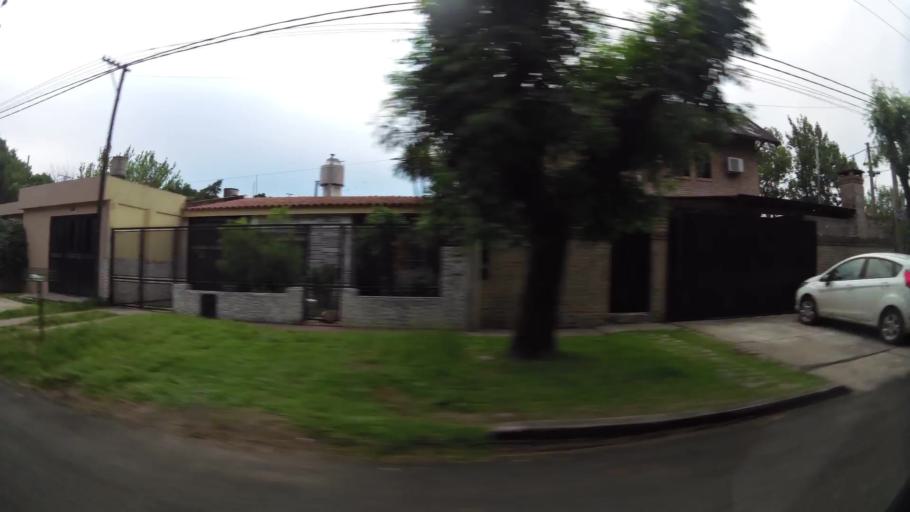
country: AR
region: Santa Fe
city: Granadero Baigorria
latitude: -32.8829
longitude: -60.7060
